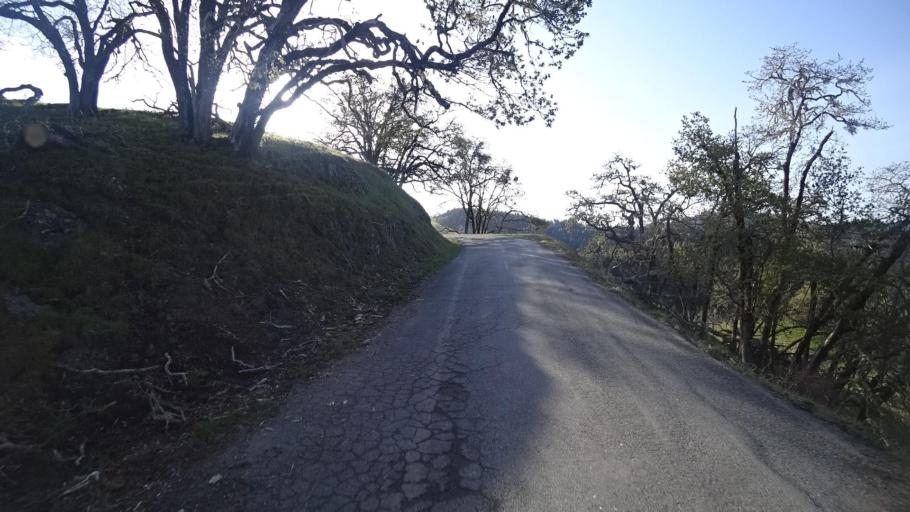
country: US
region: California
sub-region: Humboldt County
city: Blue Lake
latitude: 40.7109
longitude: -123.9395
